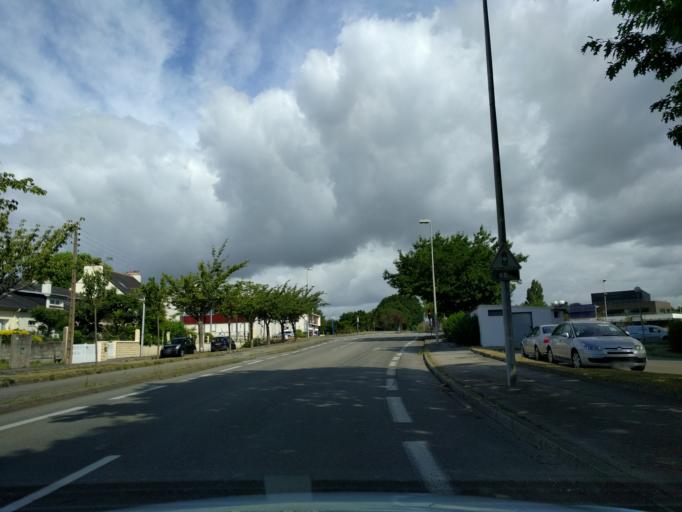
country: FR
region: Brittany
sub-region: Departement du Morbihan
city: Lorient
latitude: 47.7468
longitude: -3.3921
